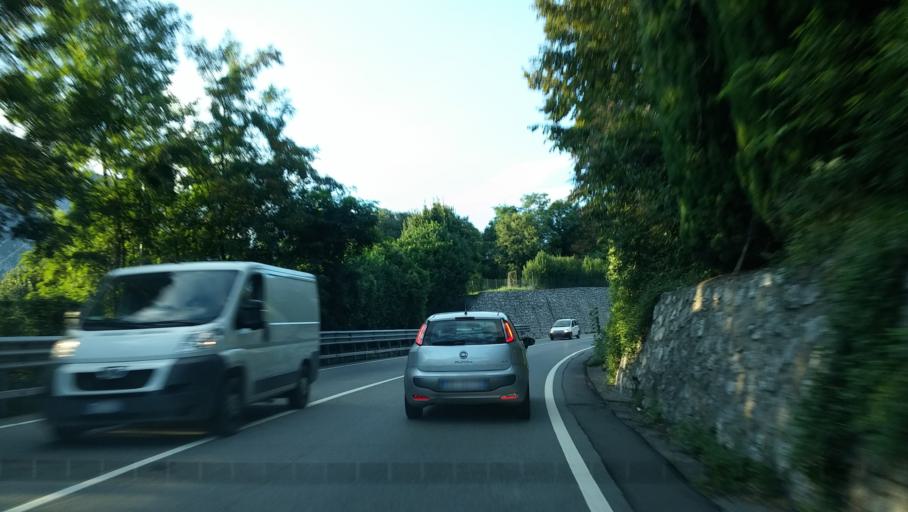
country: IT
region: Lombardy
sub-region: Provincia di Lecco
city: Lecco
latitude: 45.8612
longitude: 9.4150
